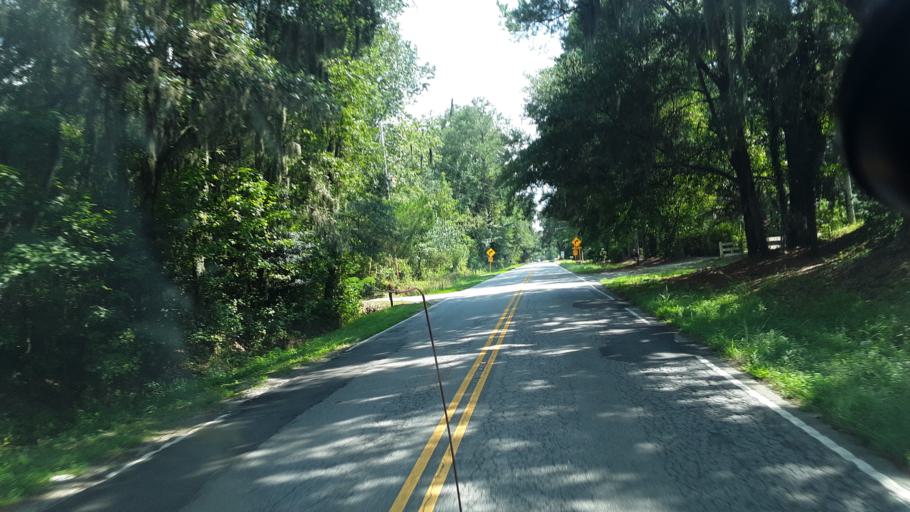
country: US
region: South Carolina
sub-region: Jasper County
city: Hardeeville
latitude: 32.1834
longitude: -81.0293
